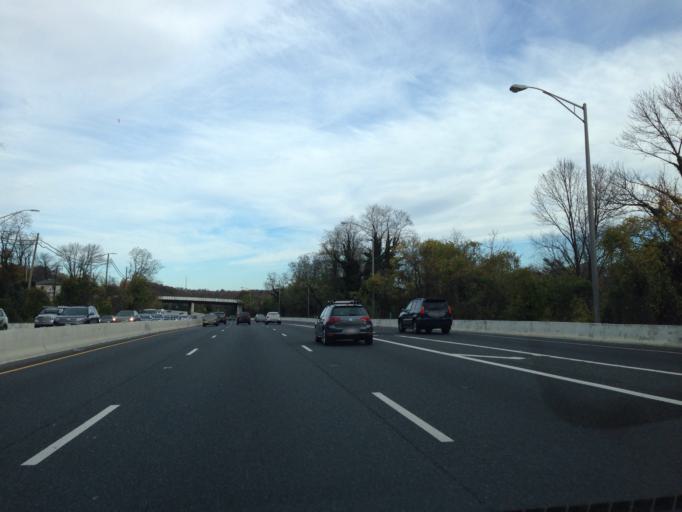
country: US
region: Maryland
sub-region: Baltimore County
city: Towson
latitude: 39.3644
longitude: -76.6501
